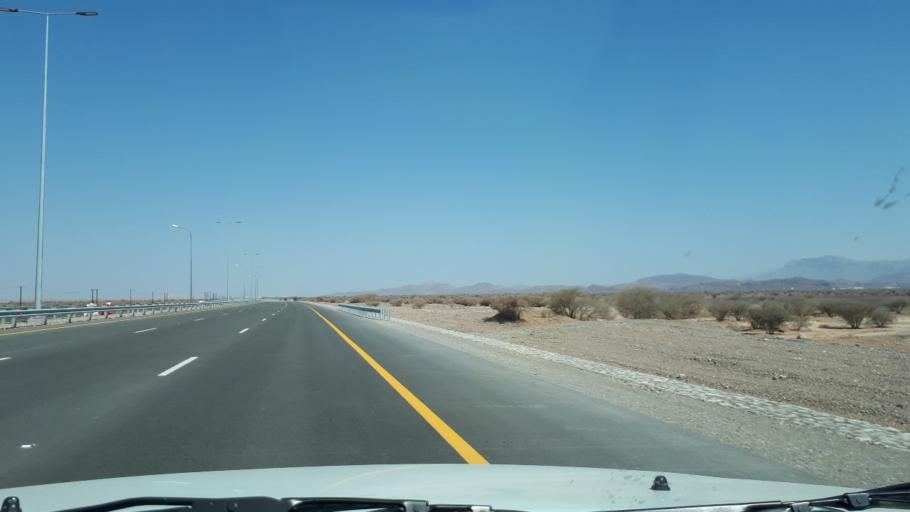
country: OM
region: Ash Sharqiyah
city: Badiyah
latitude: 22.4140
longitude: 59.0545
